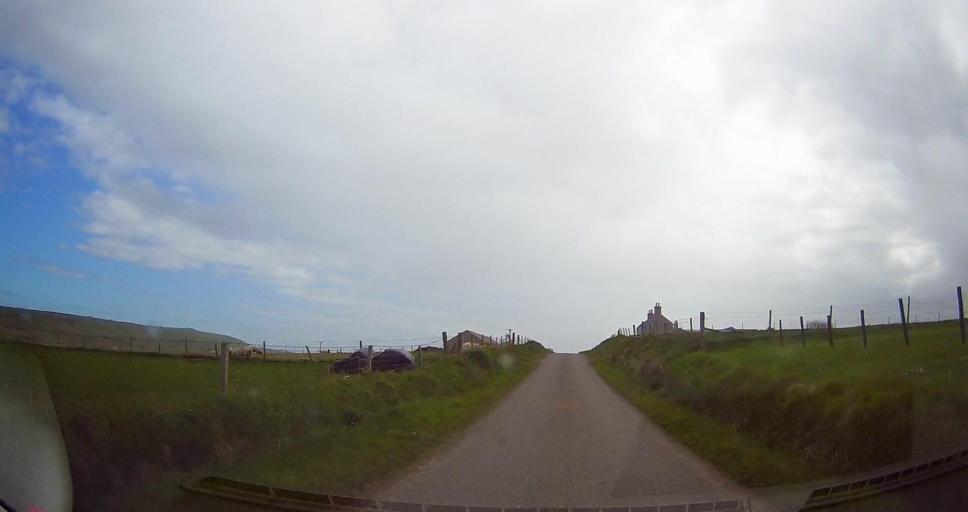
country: GB
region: Scotland
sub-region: Shetland Islands
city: Sandwick
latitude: 59.9099
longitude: -1.3348
